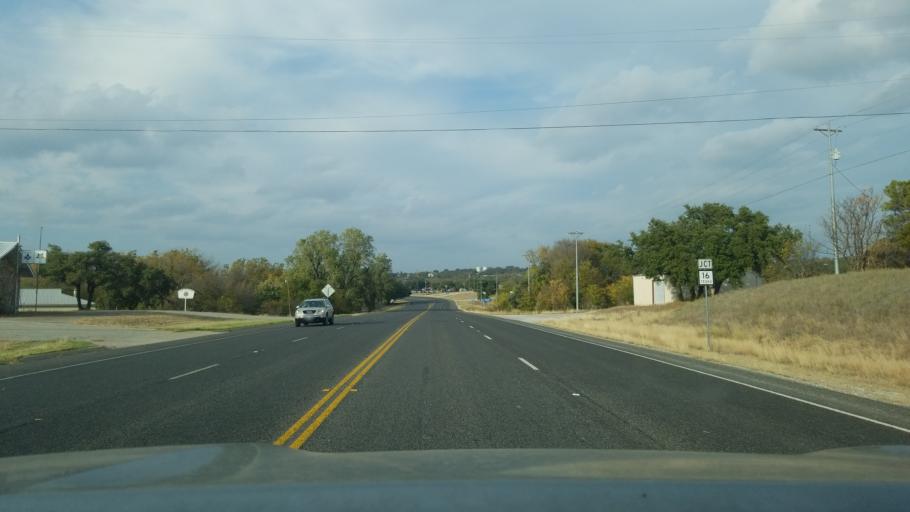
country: US
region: Texas
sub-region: Mills County
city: Goldthwaite
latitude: 31.4418
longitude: -98.5679
